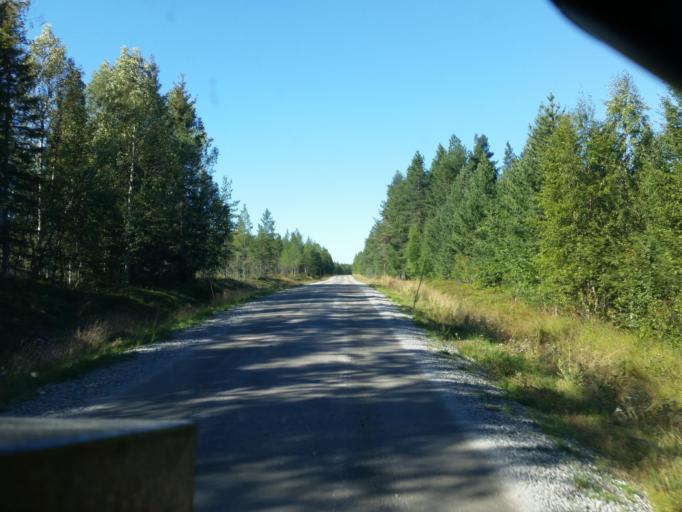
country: SE
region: Vaesterbotten
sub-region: Skelleftea Kommun
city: Storvik
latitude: 65.2158
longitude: 20.8731
